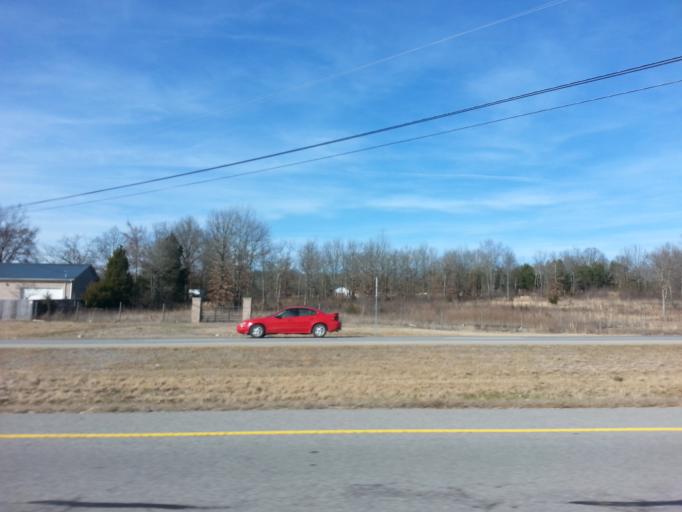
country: US
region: Tennessee
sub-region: Rutherford County
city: Murfreesboro
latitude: 35.8256
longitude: -86.2810
